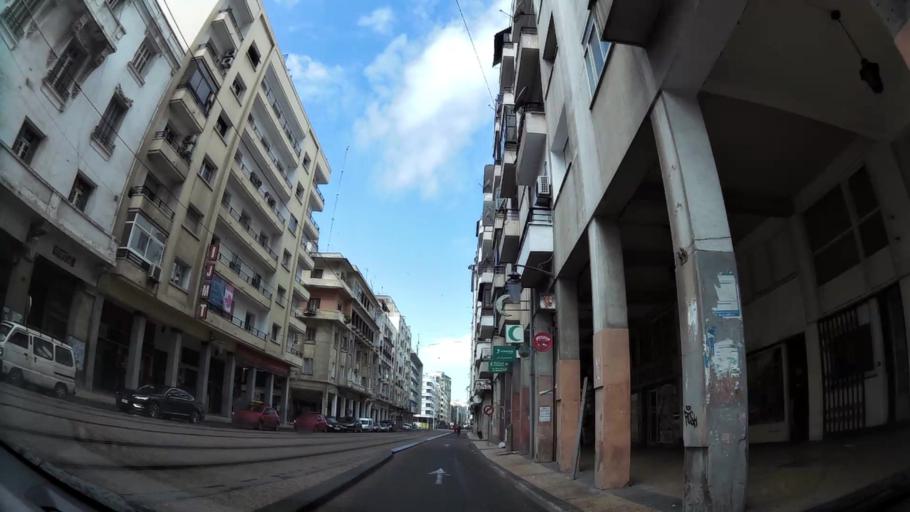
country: MA
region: Grand Casablanca
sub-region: Casablanca
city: Casablanca
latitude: 33.5936
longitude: -7.6040
